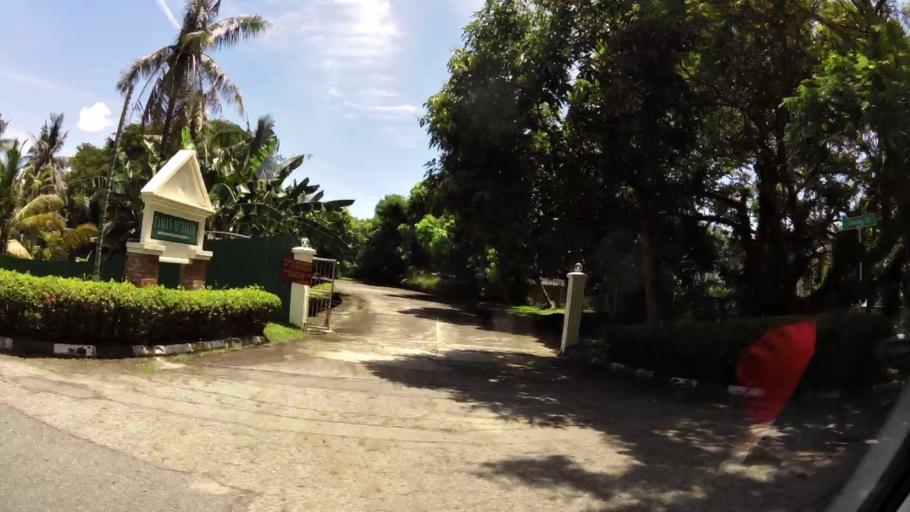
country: BN
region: Brunei and Muara
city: Bandar Seri Begawan
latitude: 4.9332
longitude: 114.9470
